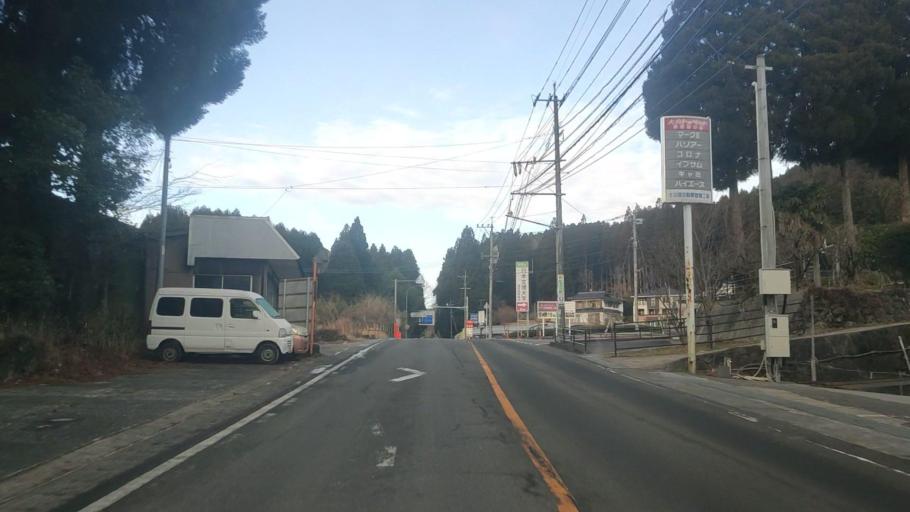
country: JP
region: Oita
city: Beppu
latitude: 33.2658
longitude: 131.3521
